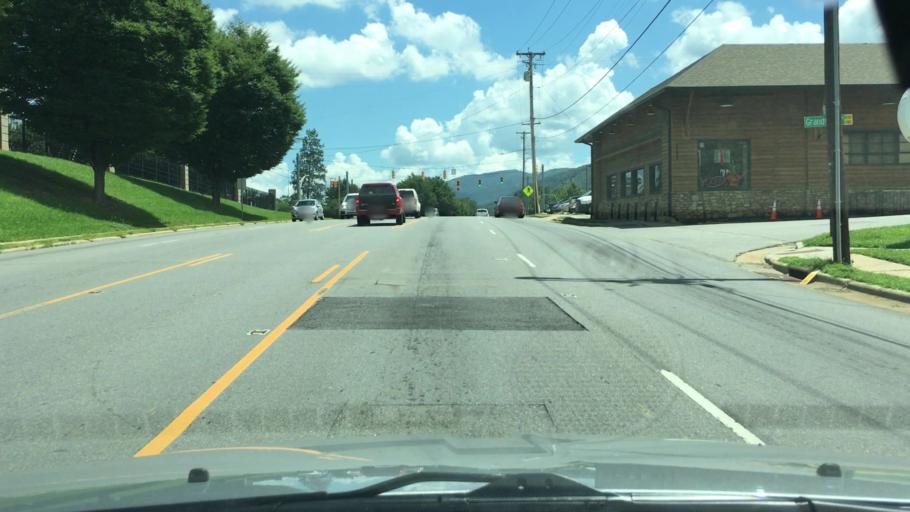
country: US
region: North Carolina
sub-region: Buncombe County
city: Biltmore Forest
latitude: 35.5874
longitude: -82.4869
